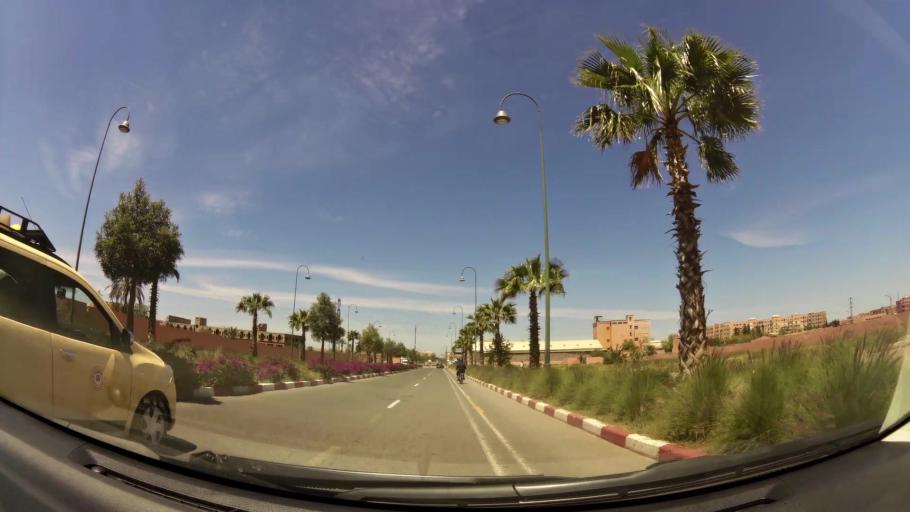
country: MA
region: Marrakech-Tensift-Al Haouz
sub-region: Marrakech
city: Marrakesh
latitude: 31.6224
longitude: -8.0223
